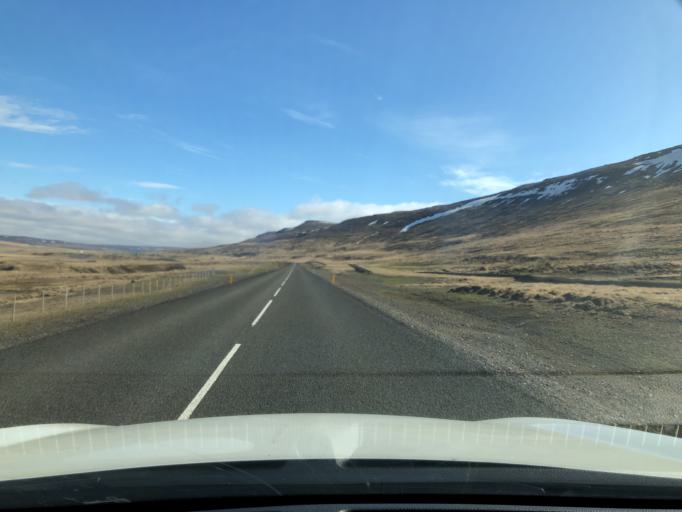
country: IS
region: West
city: Borgarnes
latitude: 65.1531
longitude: -21.5563
